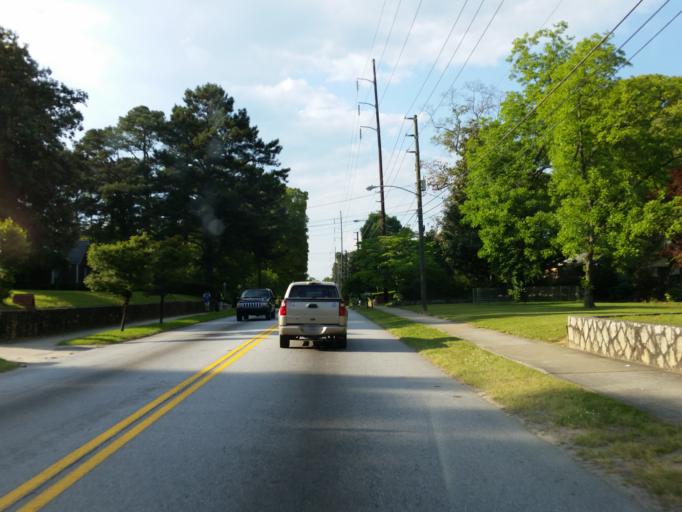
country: US
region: Georgia
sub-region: Fulton County
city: Atlanta
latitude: 33.7721
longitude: -84.4735
